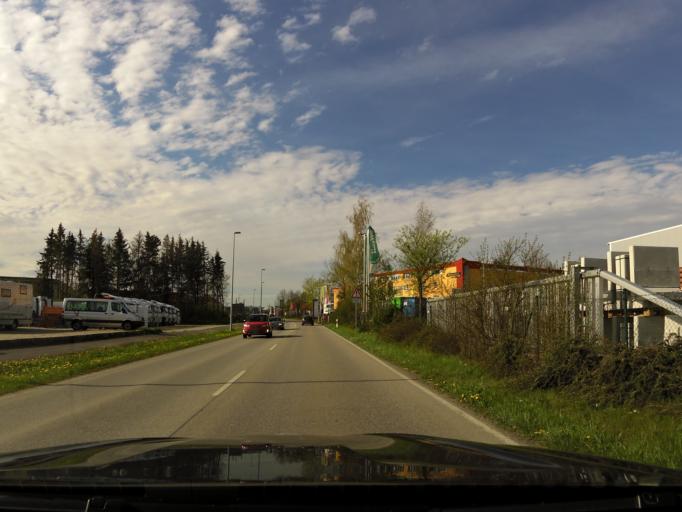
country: DE
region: Bavaria
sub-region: Upper Bavaria
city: Erding
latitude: 48.3139
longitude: 11.8920
